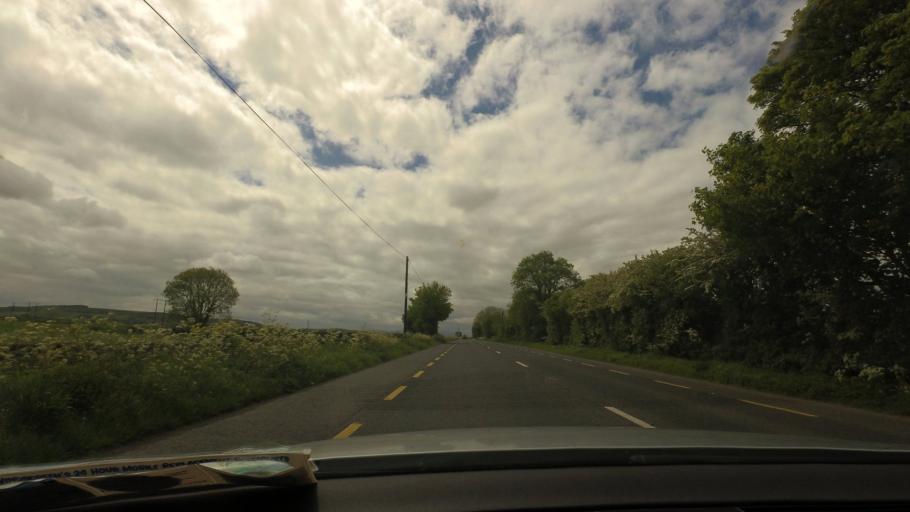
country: IE
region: Munster
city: Cashel
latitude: 52.5755
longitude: -7.8327
